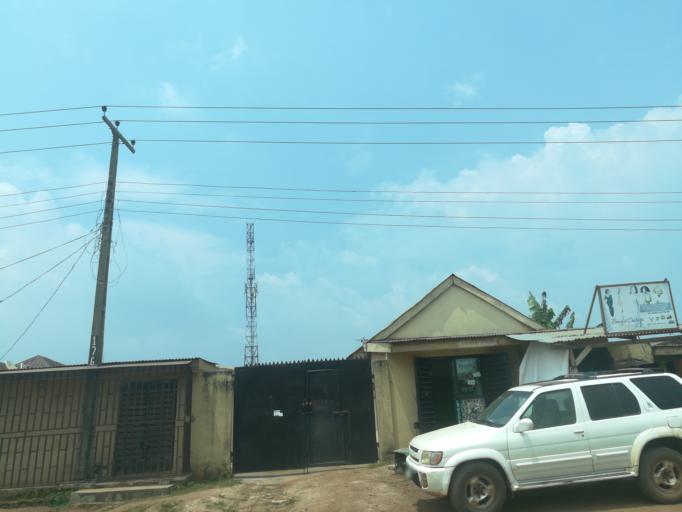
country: NG
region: Lagos
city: Ikorodu
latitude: 6.6042
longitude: 3.6026
